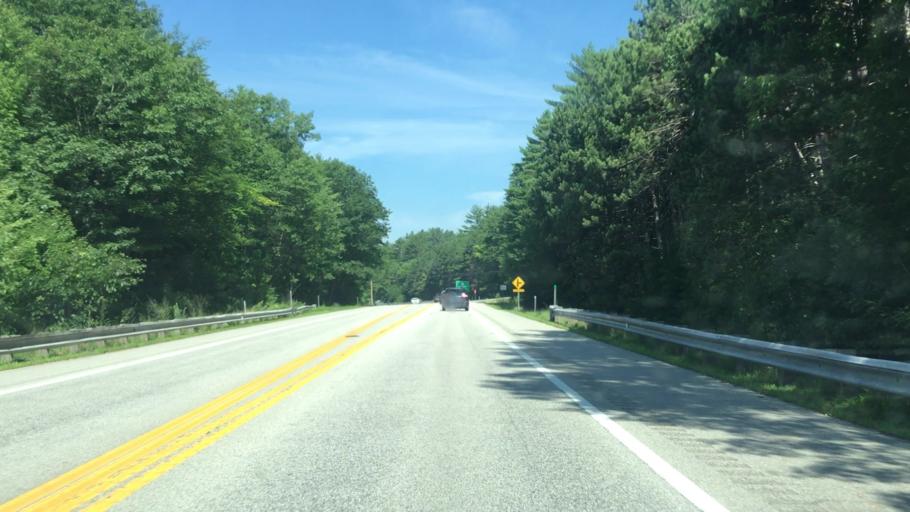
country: US
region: New Hampshire
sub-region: Merrimack County
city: Henniker
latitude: 43.1889
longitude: -71.8090
